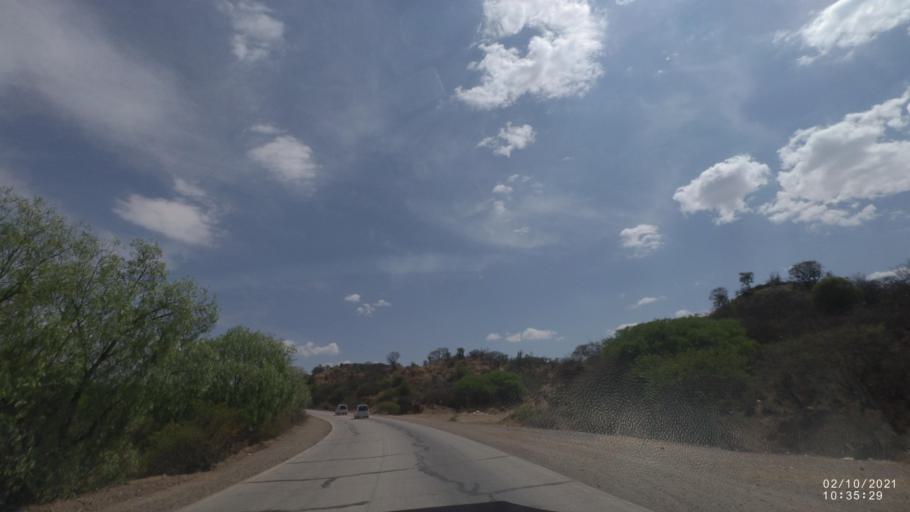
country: BO
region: Cochabamba
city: Capinota
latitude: -17.6605
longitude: -66.2575
